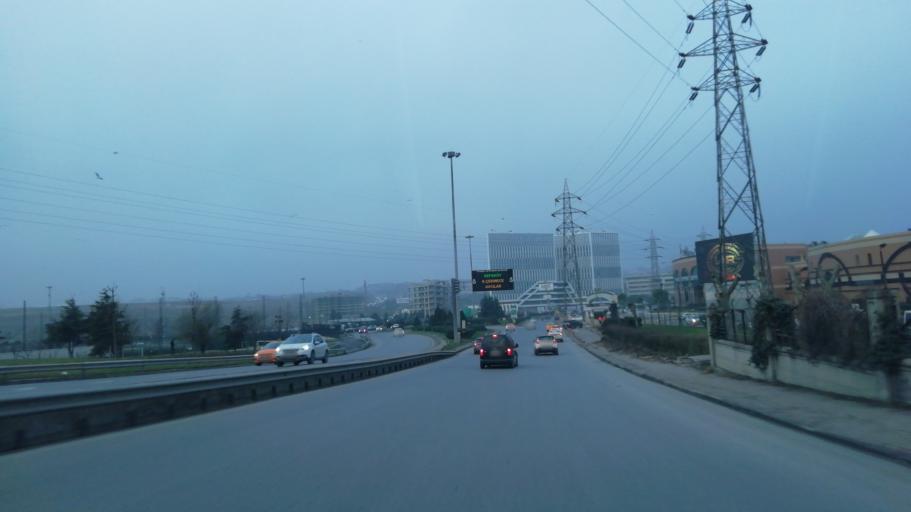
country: TR
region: Istanbul
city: Bahcelievler
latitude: 41.0007
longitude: 28.8197
